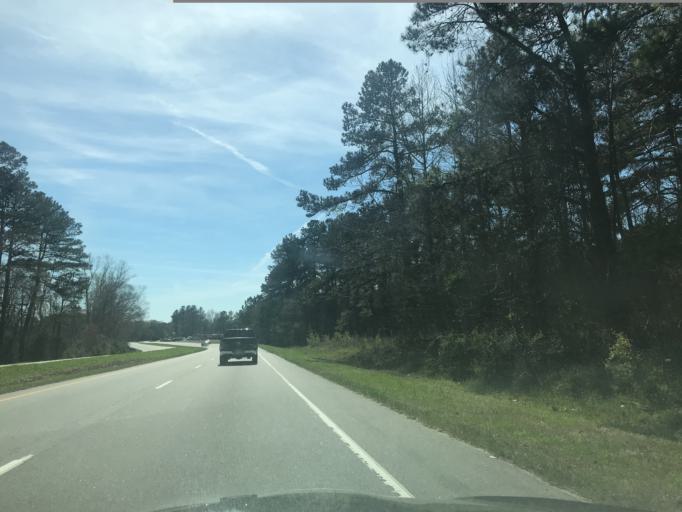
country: US
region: North Carolina
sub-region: Wake County
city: Garner
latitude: 35.6762
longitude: -78.6885
